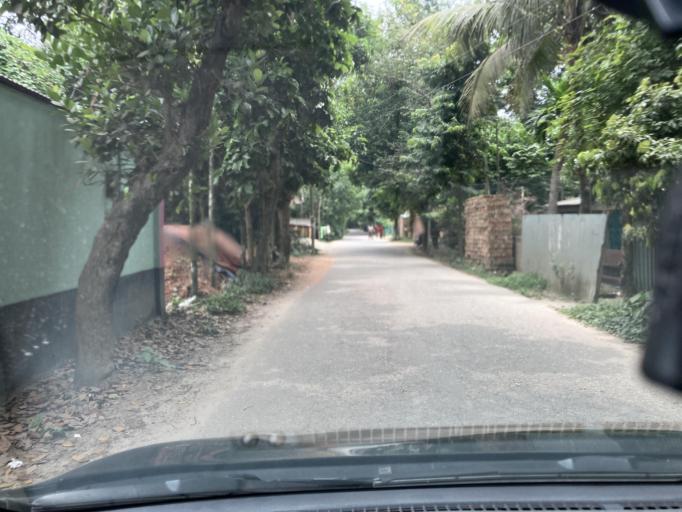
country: BD
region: Dhaka
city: Dohar
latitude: 23.8141
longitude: 90.0469
